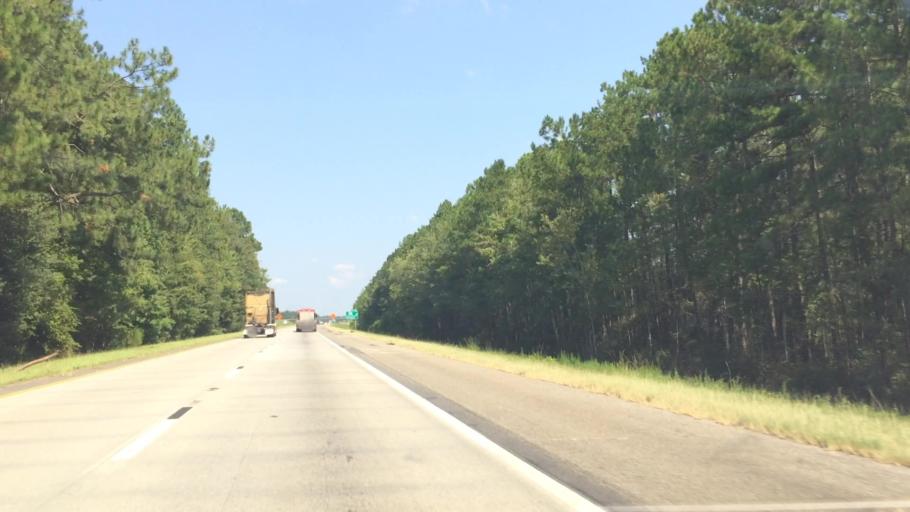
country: US
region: South Carolina
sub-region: Dorchester County
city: Saint George
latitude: 33.0758
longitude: -80.6567
